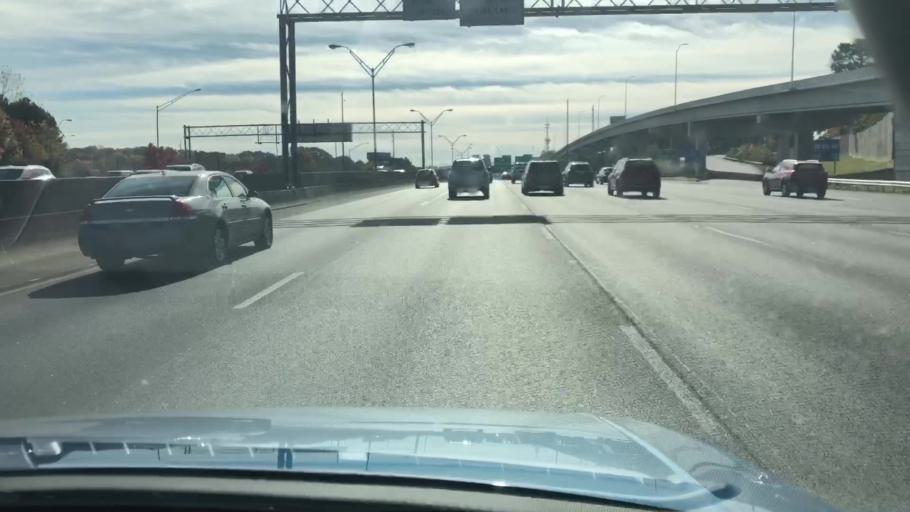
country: US
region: Georgia
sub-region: Cobb County
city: Smyrna
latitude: 33.9271
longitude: -84.4888
